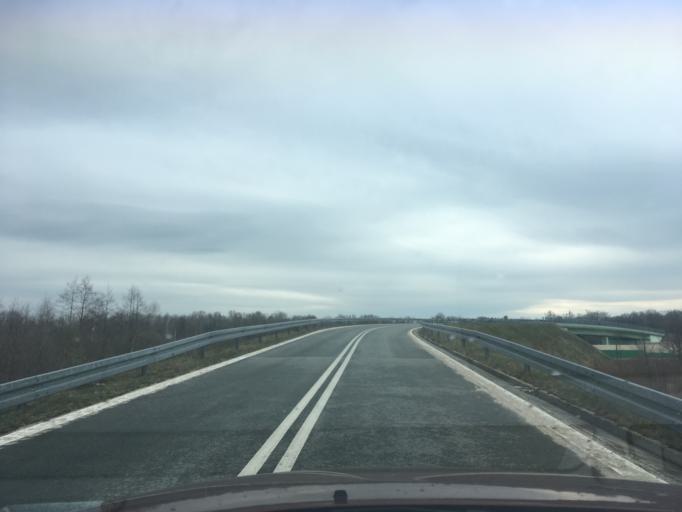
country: PL
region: Lower Silesian Voivodeship
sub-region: Powiat zgorzelecki
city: Lagow
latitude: 51.1726
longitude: 15.0442
